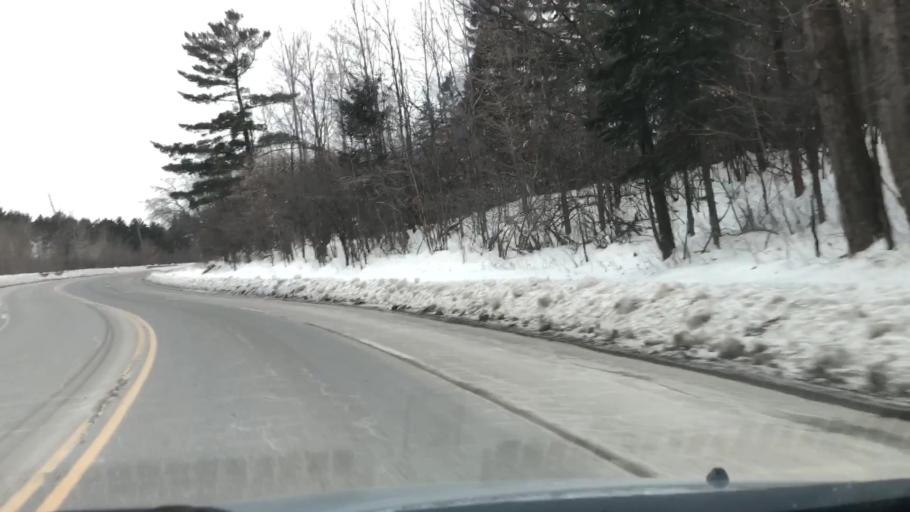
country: US
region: Minnesota
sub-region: Saint Louis County
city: Arnold
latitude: 46.8388
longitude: -92.0769
